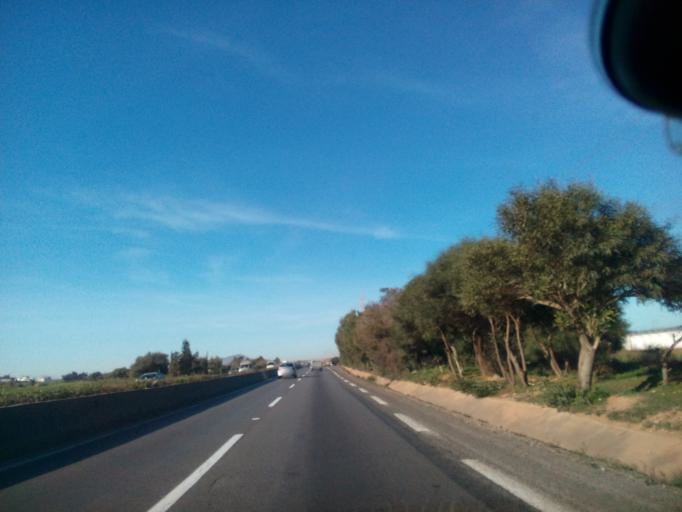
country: DZ
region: Oran
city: Ain el Bya
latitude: 35.8001
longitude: -0.3346
